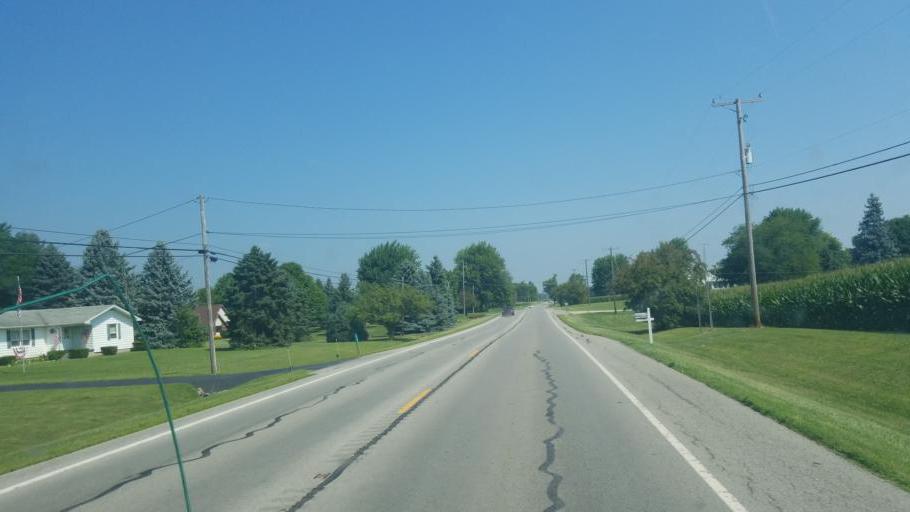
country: US
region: Ohio
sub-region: Hardin County
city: Kenton
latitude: 40.6684
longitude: -83.6108
